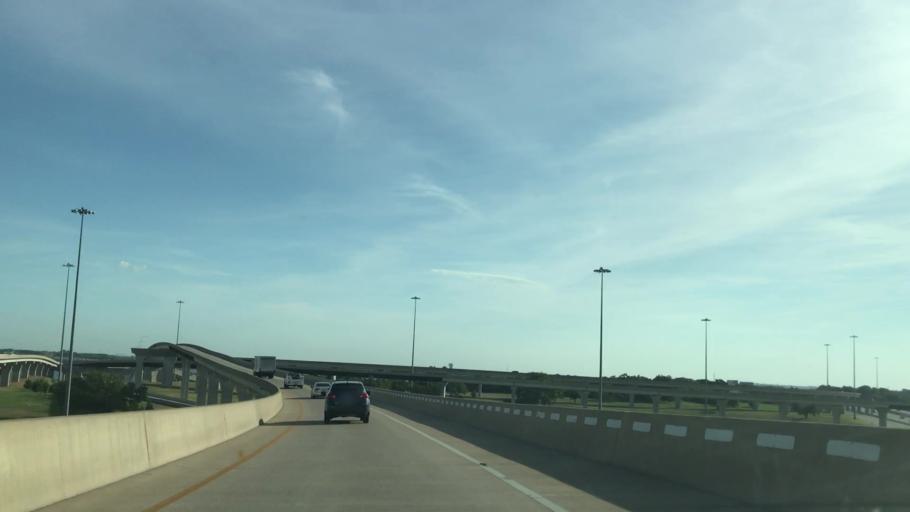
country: US
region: Texas
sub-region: Dallas County
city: Rowlett
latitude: 32.8566
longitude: -96.5565
